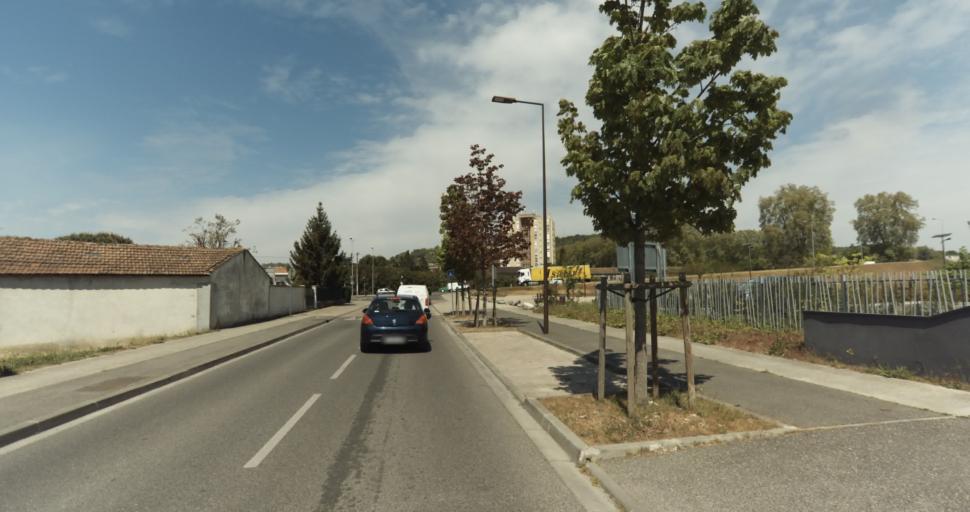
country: FR
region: Aquitaine
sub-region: Departement du Lot-et-Garonne
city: Agen
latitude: 44.2066
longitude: 0.6405
